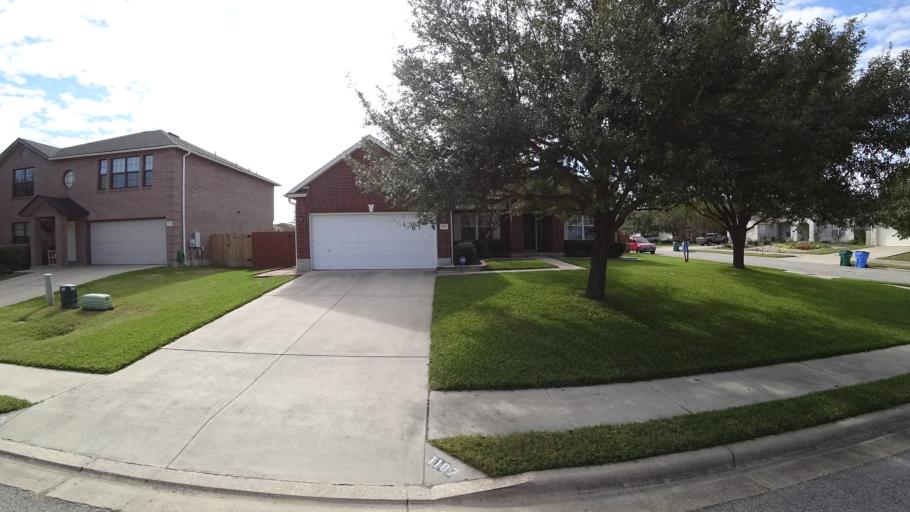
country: US
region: Texas
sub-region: Travis County
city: Pflugerville
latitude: 30.4485
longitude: -97.6264
